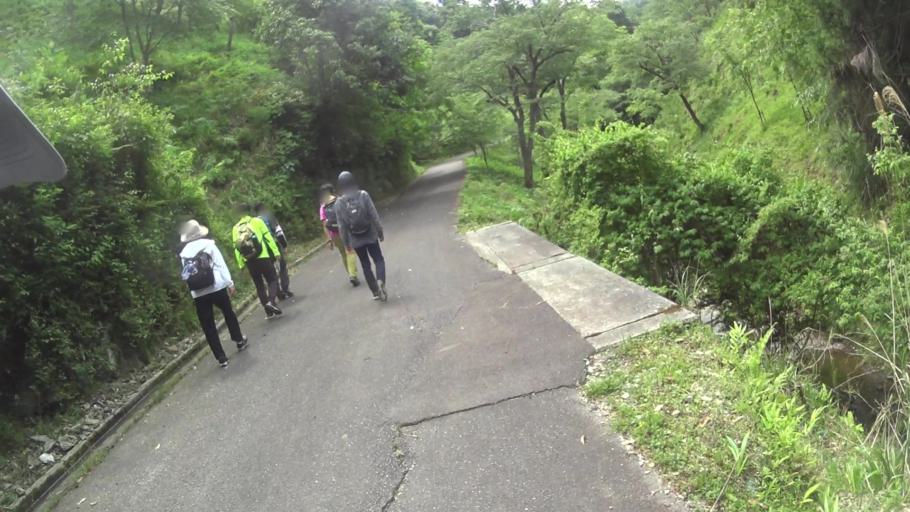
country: JP
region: Nara
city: Yoshino-cho
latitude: 34.3644
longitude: 135.8661
